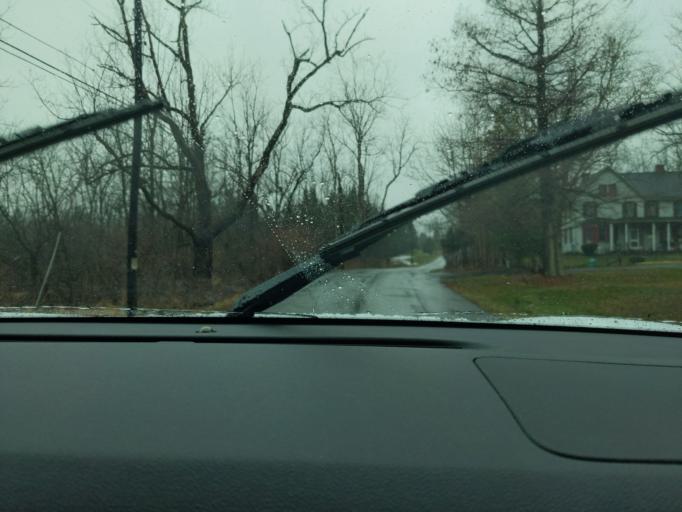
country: US
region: Pennsylvania
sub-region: Bucks County
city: Spinnerstown
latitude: 40.4311
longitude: -75.4042
